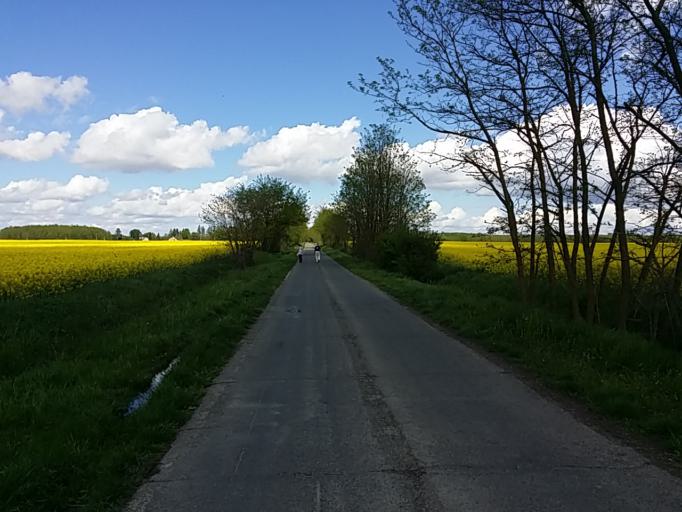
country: HR
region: Koprivnicko-Krizevacka
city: Ferdinandovac
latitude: 46.1072
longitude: 17.2448
